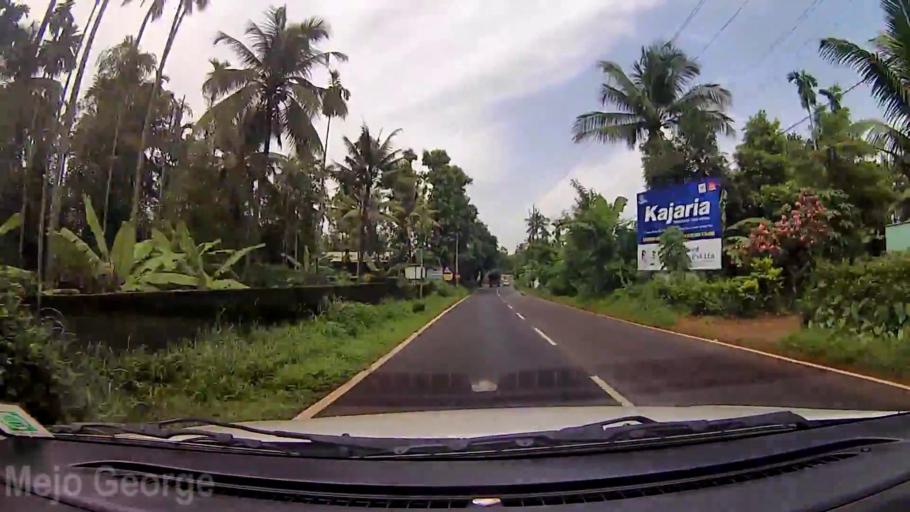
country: IN
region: Kerala
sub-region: Thrissur District
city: Kizhake Chalakudi
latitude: 10.3368
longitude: 76.3003
